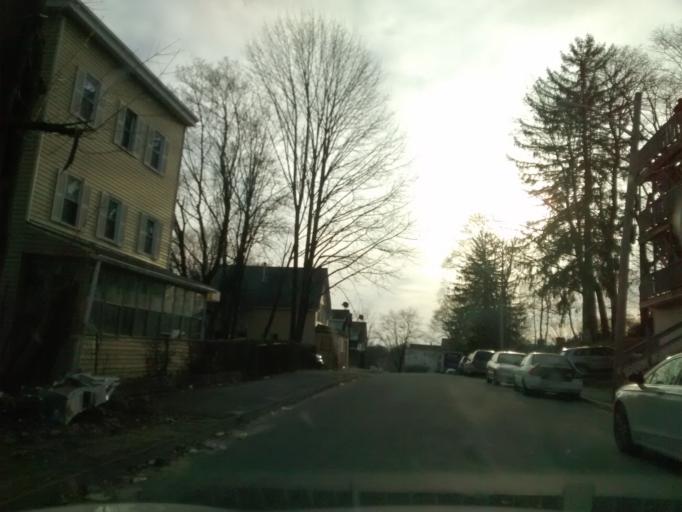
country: US
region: Massachusetts
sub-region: Worcester County
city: Worcester
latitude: 42.2838
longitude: -71.8012
